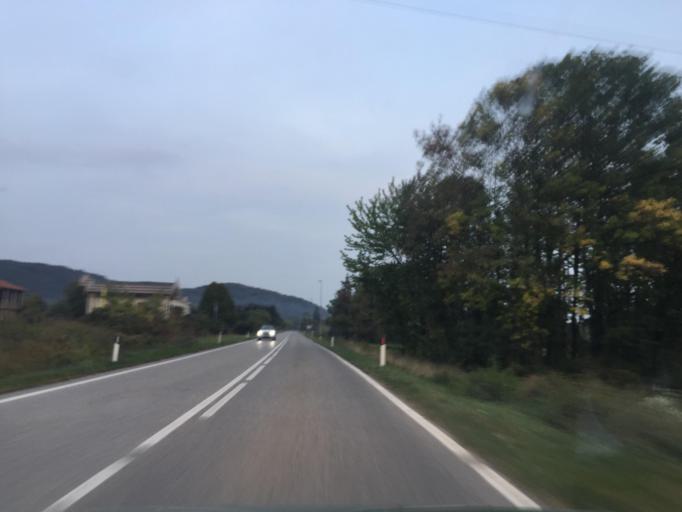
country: IT
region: Friuli Venezia Giulia
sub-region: Provincia di Pordenone
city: Arba
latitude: 46.1623
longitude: 12.7993
